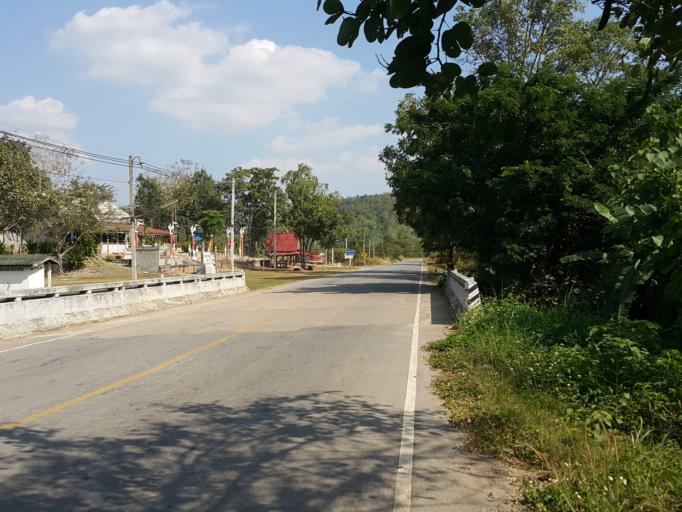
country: TH
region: Sukhothai
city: Thung Saliam
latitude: 17.3426
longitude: 99.4654
